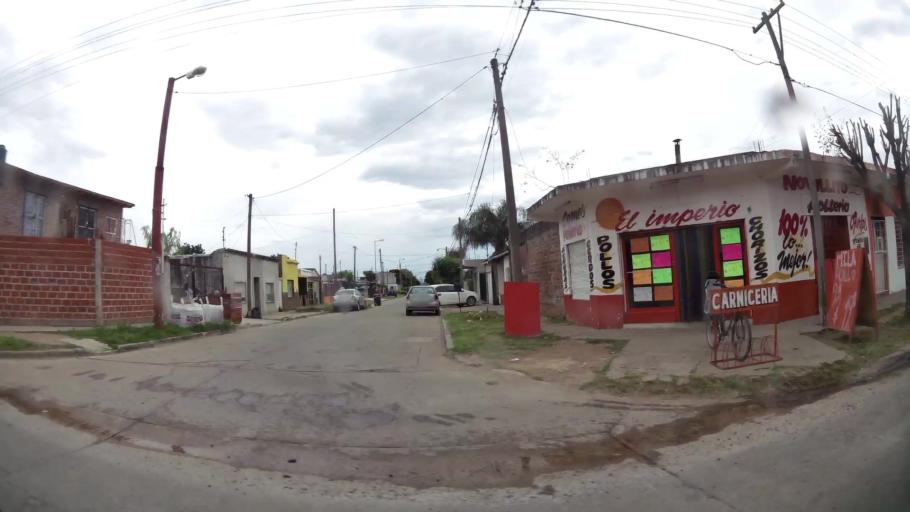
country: AR
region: Buenos Aires
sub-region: Partido de Zarate
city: Zarate
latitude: -34.0928
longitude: -59.0402
